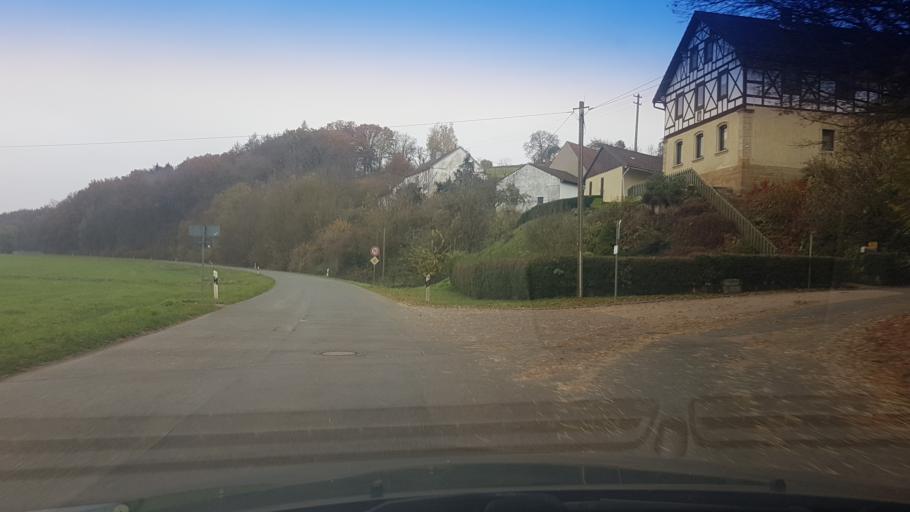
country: DE
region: Bavaria
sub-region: Upper Franconia
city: Rattelsdorf
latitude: 50.0461
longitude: 10.8718
